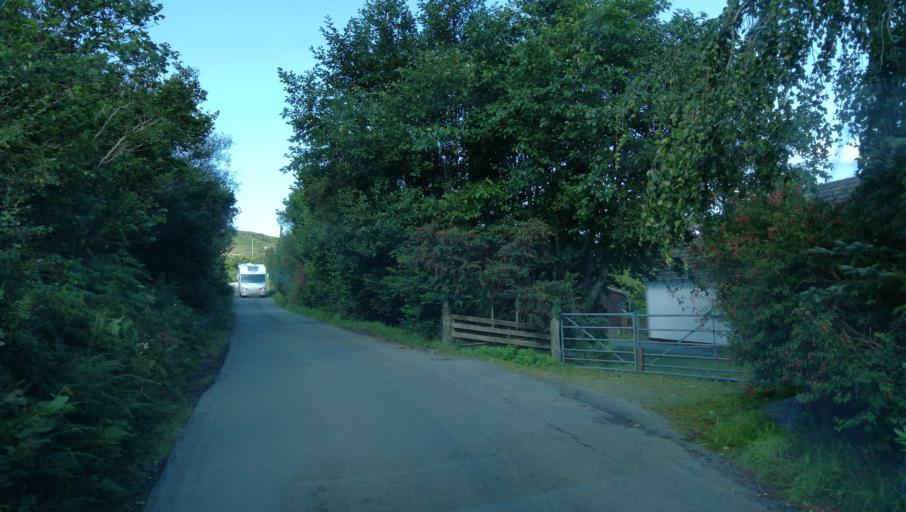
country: GB
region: Scotland
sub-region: Highland
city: Isle of Skye
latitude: 57.4477
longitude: -6.6470
